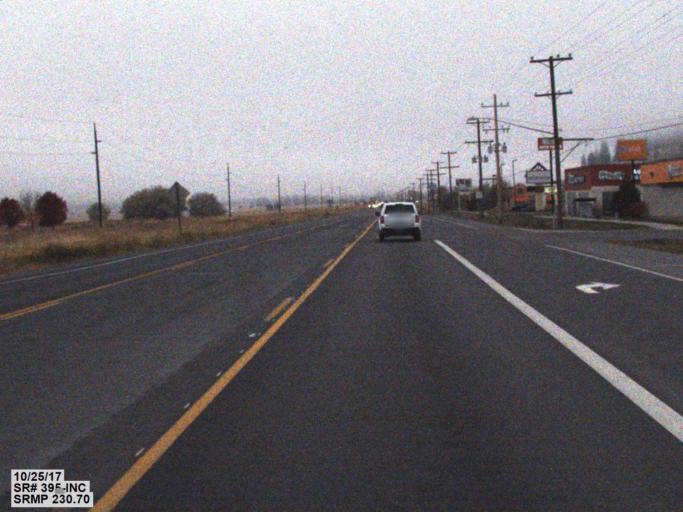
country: US
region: Washington
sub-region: Stevens County
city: Colville
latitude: 48.5559
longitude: -117.9219
